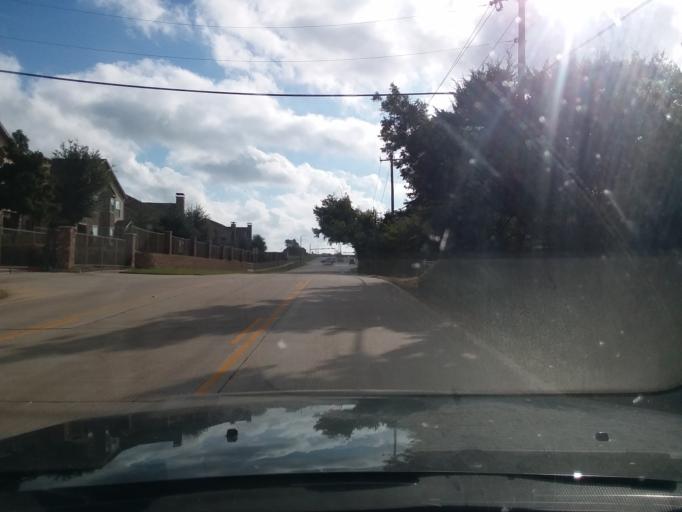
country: US
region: Texas
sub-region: Denton County
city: Hickory Creek
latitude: 33.1226
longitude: -97.0408
